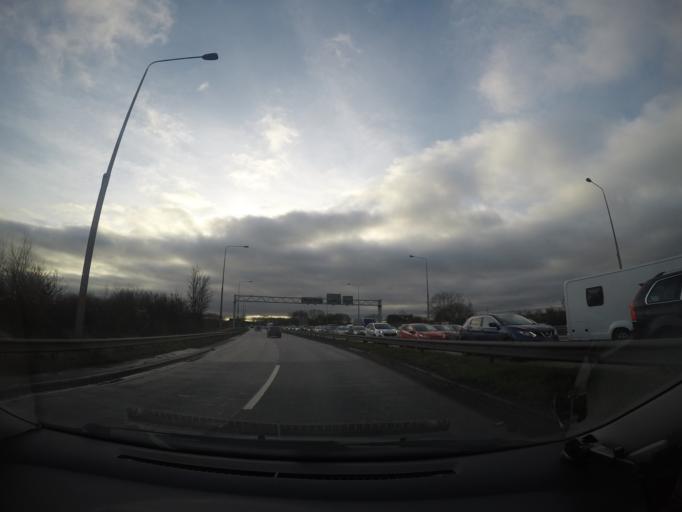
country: GB
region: England
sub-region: City of York
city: Murton
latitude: 53.9892
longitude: -1.0231
